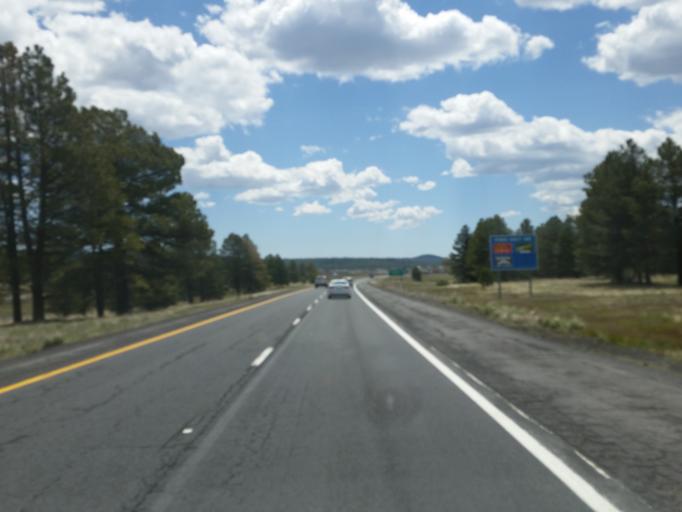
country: US
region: Arizona
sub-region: Coconino County
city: Parks
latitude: 35.2452
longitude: -111.8436
